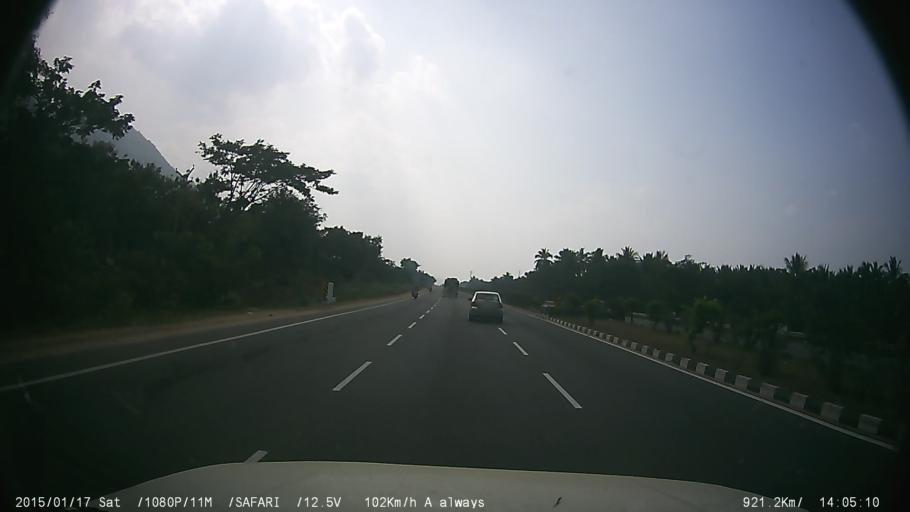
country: IN
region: Tamil Nadu
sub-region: Vellore
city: Odugattur
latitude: 12.8503
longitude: 78.8103
